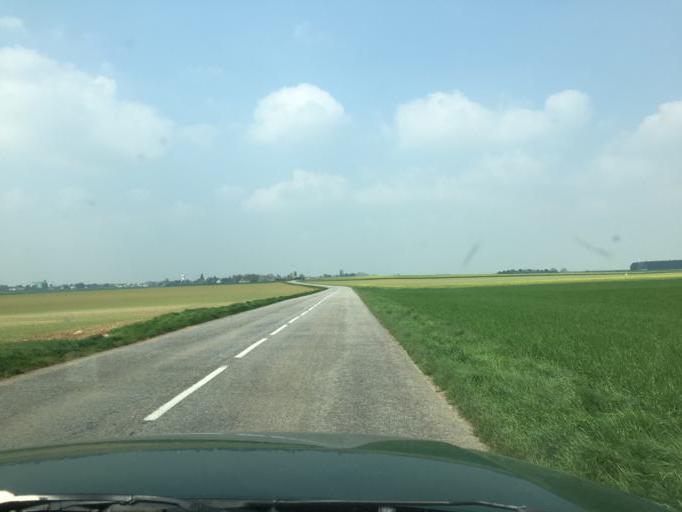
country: FR
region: Centre
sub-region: Departement du Loiret
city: Beaugency
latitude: 47.8222
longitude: 1.5947
